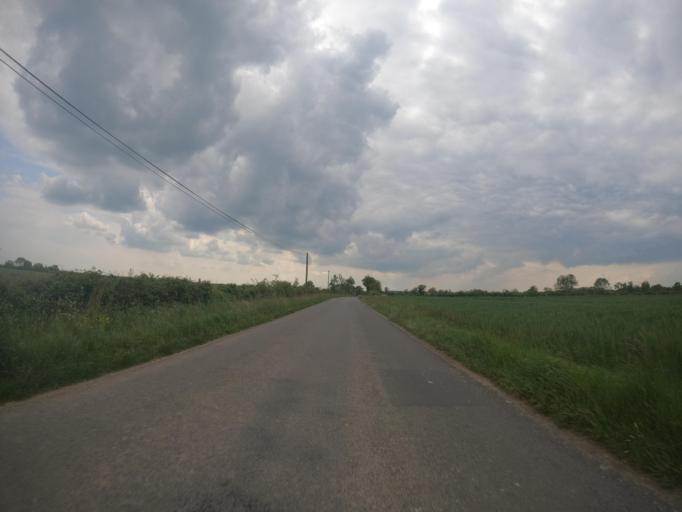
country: FR
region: Poitou-Charentes
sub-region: Departement des Deux-Sevres
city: Chiche
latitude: 46.8602
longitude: -0.3086
